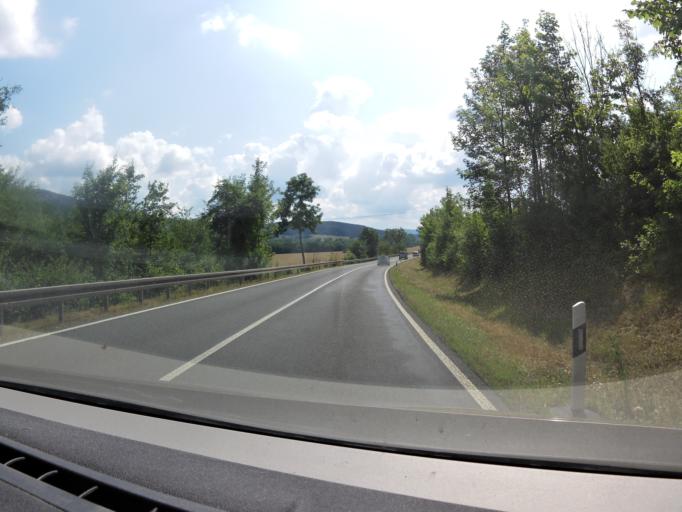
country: DE
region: Thuringia
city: Plaue
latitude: 50.7935
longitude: 10.9107
